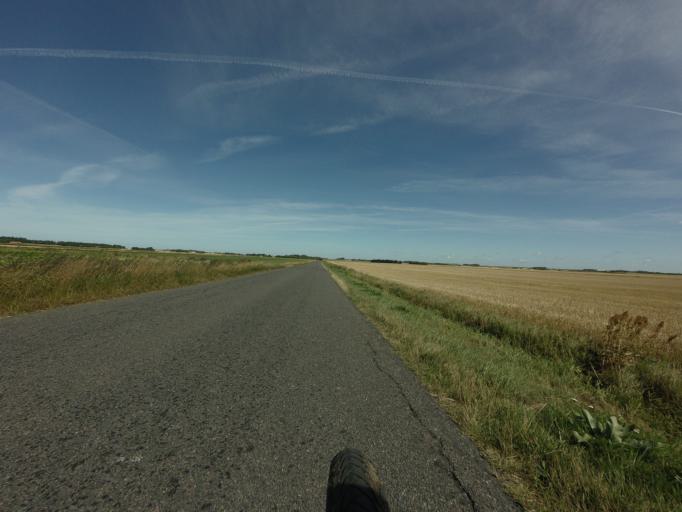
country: DK
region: North Denmark
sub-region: Bronderslev Kommune
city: Bronderslev
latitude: 57.3100
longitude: 9.8100
